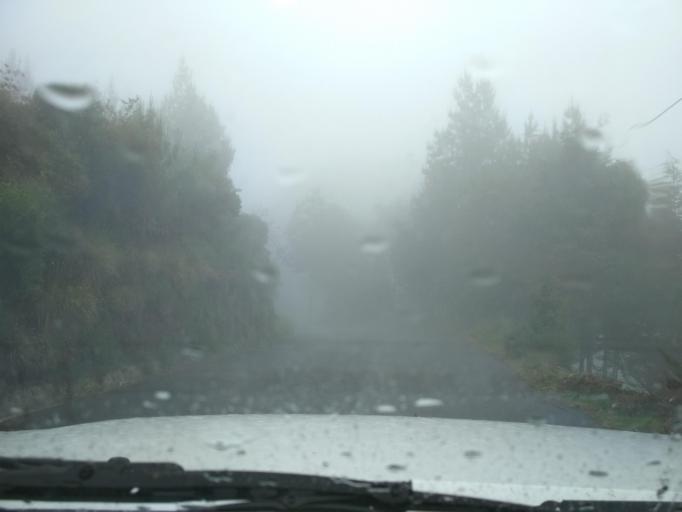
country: MX
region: Veracruz
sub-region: Mariano Escobedo
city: San Isidro el Berro
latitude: 18.9306
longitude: -97.2124
